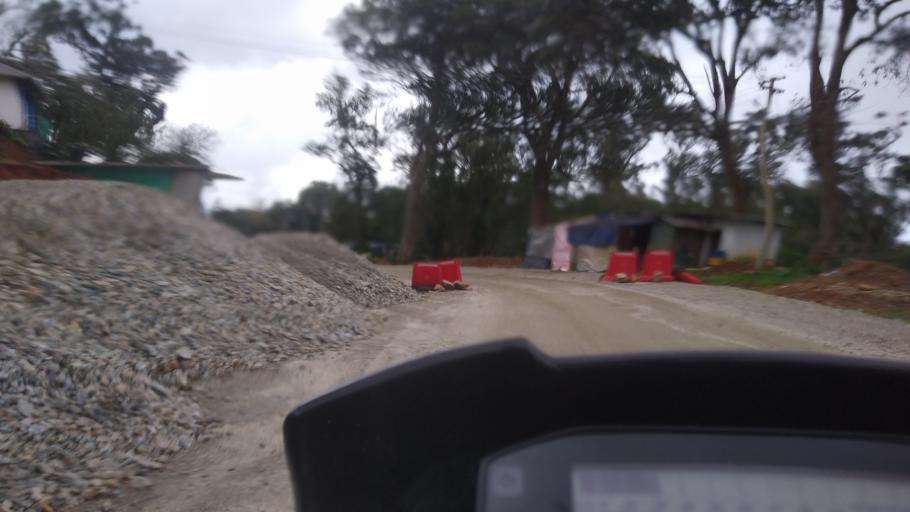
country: IN
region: Kerala
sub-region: Idukki
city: Munnar
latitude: 10.0347
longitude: 77.1498
